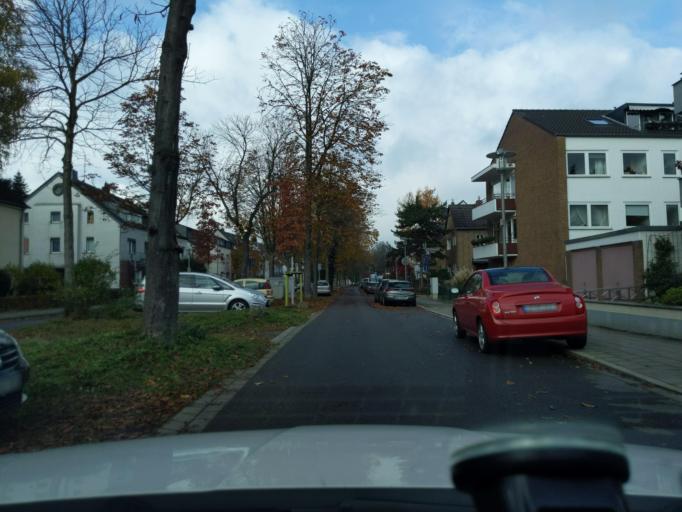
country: DE
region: North Rhine-Westphalia
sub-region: Regierungsbezirk Dusseldorf
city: Dusseldorf
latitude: 51.2385
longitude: 6.8333
